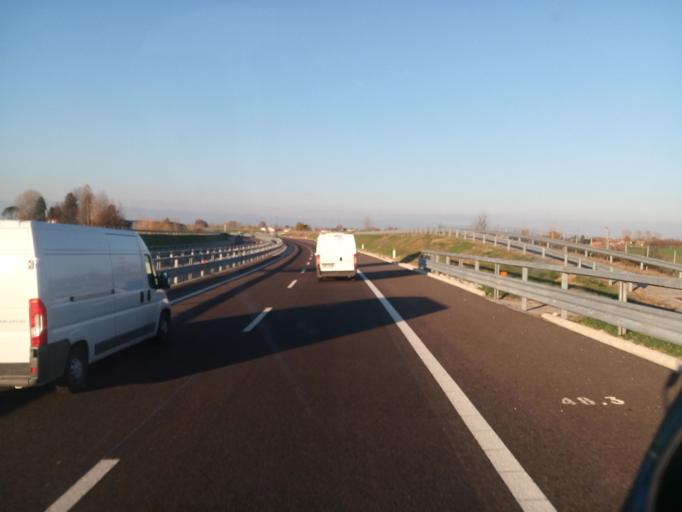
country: IT
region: Veneto
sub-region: Provincia di Vicenza
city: Longare
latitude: 45.4664
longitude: 11.6350
